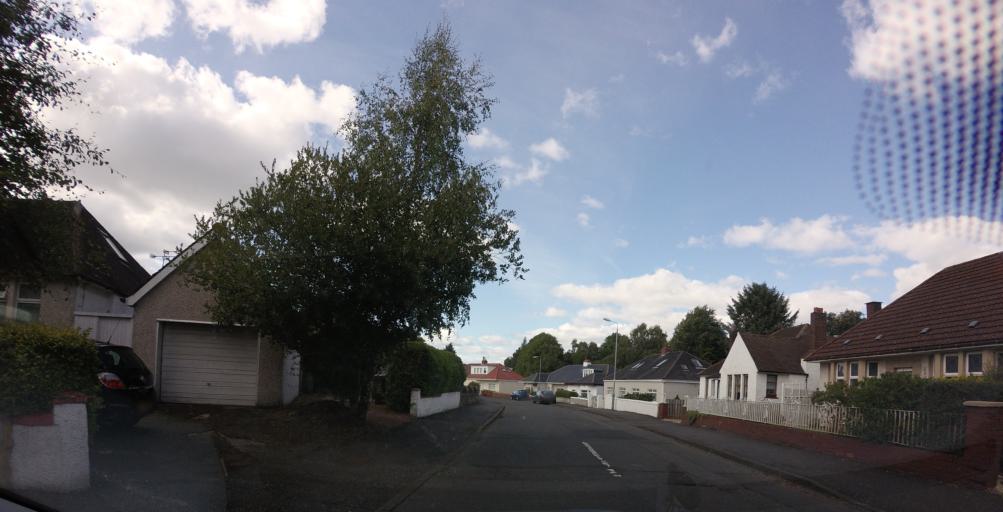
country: GB
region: Scotland
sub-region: North Lanarkshire
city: Coatbridge
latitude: 55.8598
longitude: -4.0464
